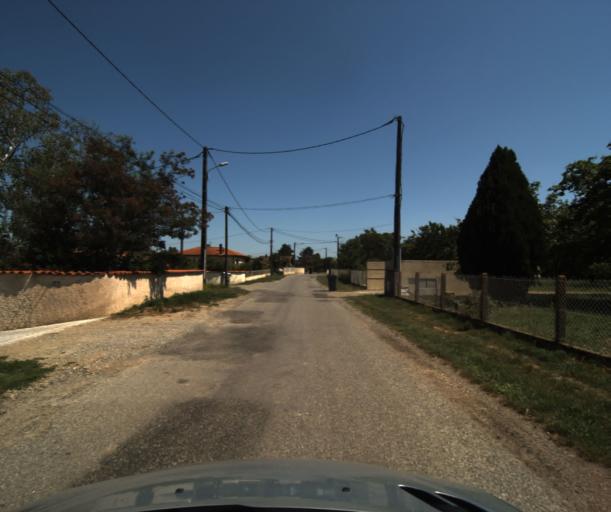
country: FR
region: Midi-Pyrenees
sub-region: Departement de la Haute-Garonne
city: Saubens
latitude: 43.4751
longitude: 1.3612
